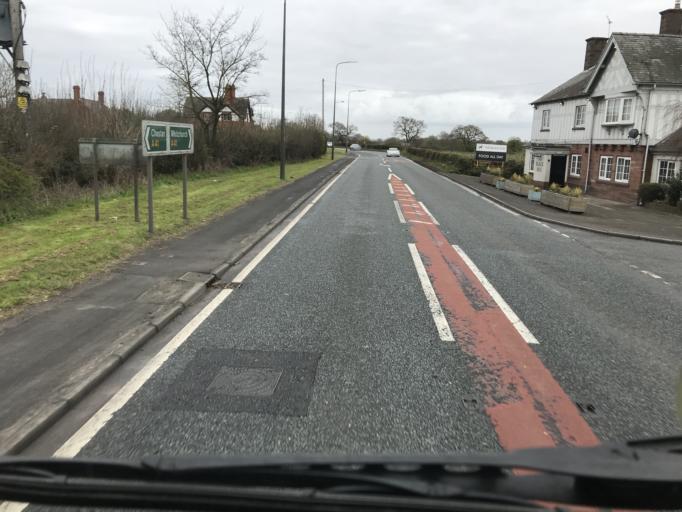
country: GB
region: England
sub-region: Cheshire West and Chester
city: Waverton
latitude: 53.1670
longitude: -2.8202
